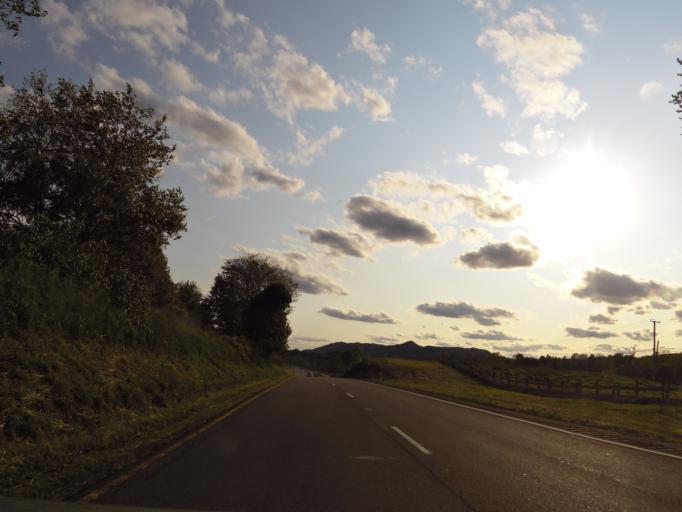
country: US
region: Virginia
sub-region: Russell County
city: Honaker
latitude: 36.9683
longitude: -81.9114
